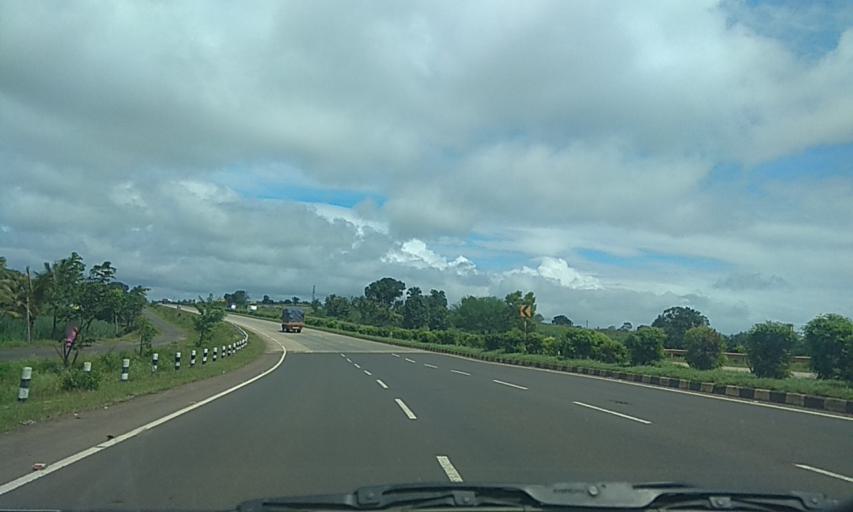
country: IN
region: Karnataka
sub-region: Dharwad
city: Alnavar
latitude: 15.6243
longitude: 74.7586
